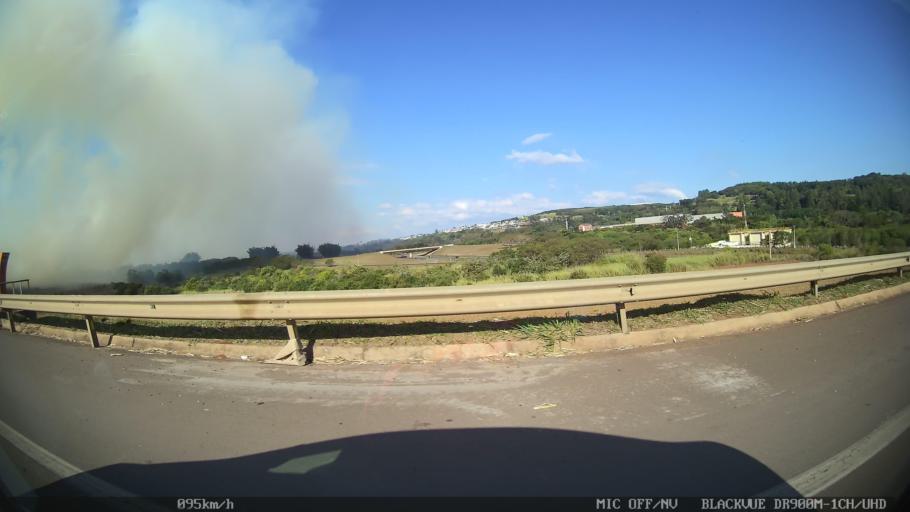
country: BR
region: Sao Paulo
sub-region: Piracicaba
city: Piracicaba
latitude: -22.6981
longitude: -47.6062
